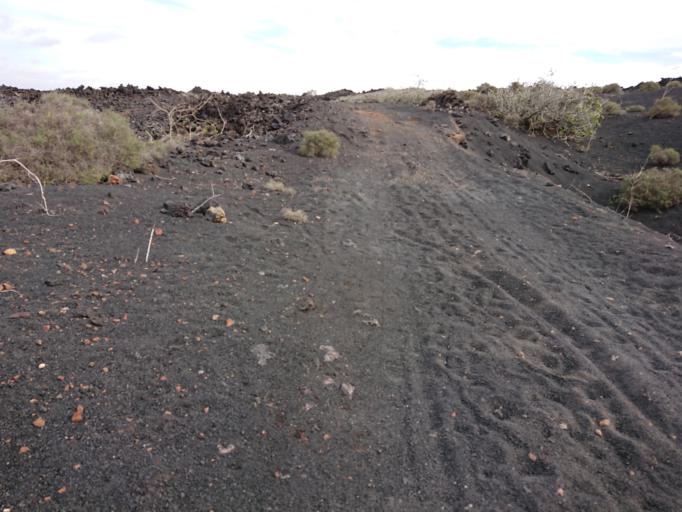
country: ES
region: Canary Islands
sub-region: Provincia de Las Palmas
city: Tinajo
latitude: 29.0132
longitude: -13.6781
